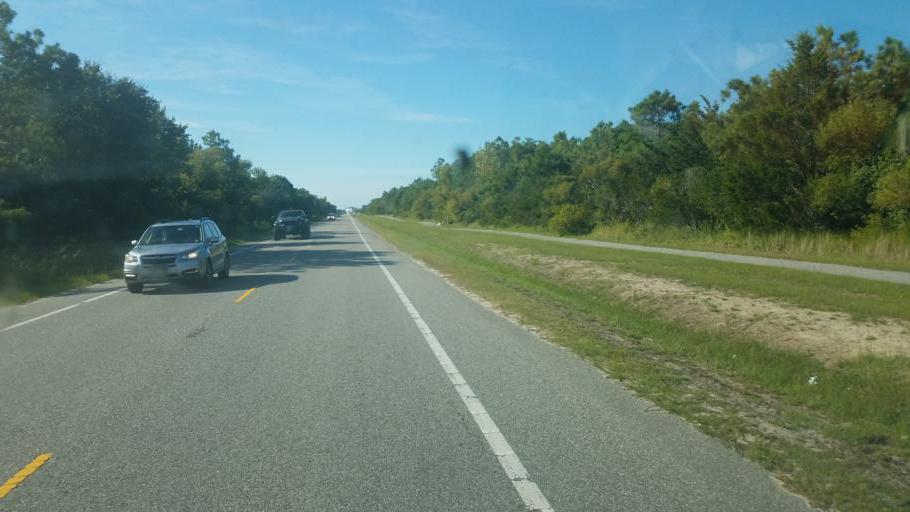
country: US
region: North Carolina
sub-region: Dare County
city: Southern Shores
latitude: 36.3404
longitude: -75.8194
